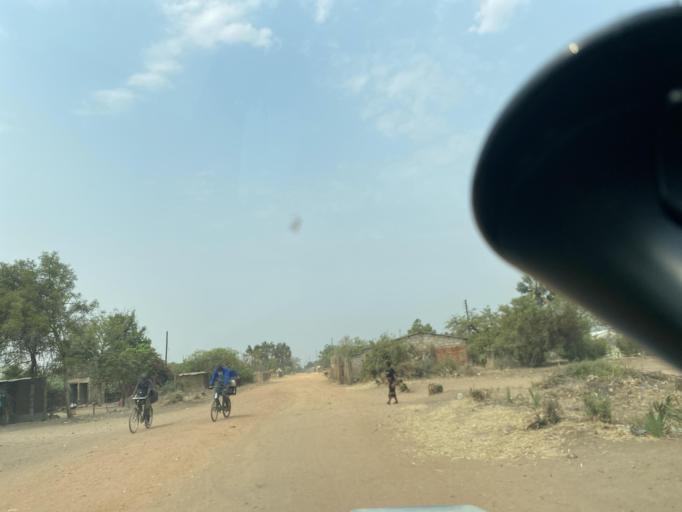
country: ZM
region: Lusaka
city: Kafue
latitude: -15.6660
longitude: 28.0192
